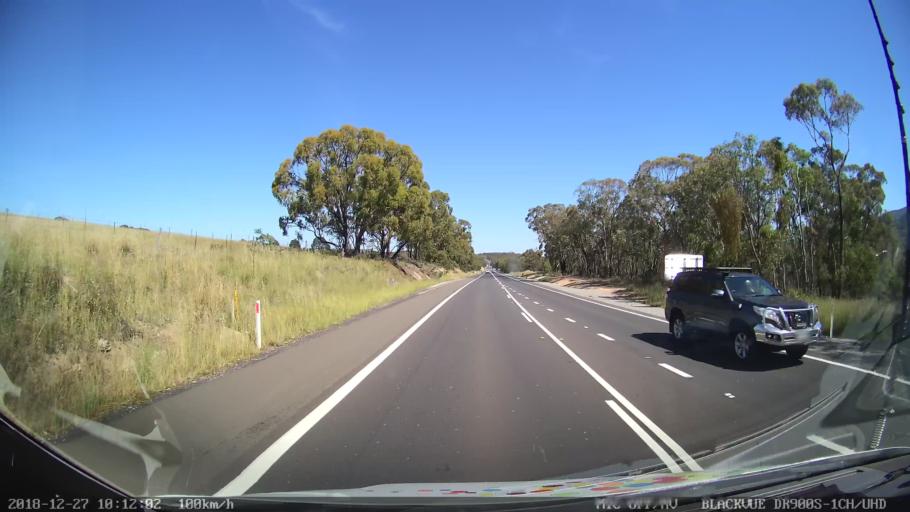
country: AU
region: New South Wales
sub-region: Bathurst Regional
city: Kelso
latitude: -33.4476
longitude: 149.7653
